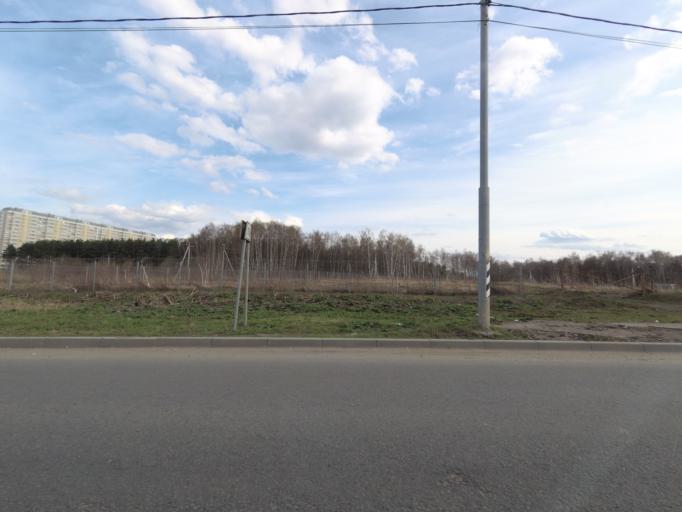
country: RU
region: Moskovskaya
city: Lobnya
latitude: 56.0063
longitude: 37.4351
